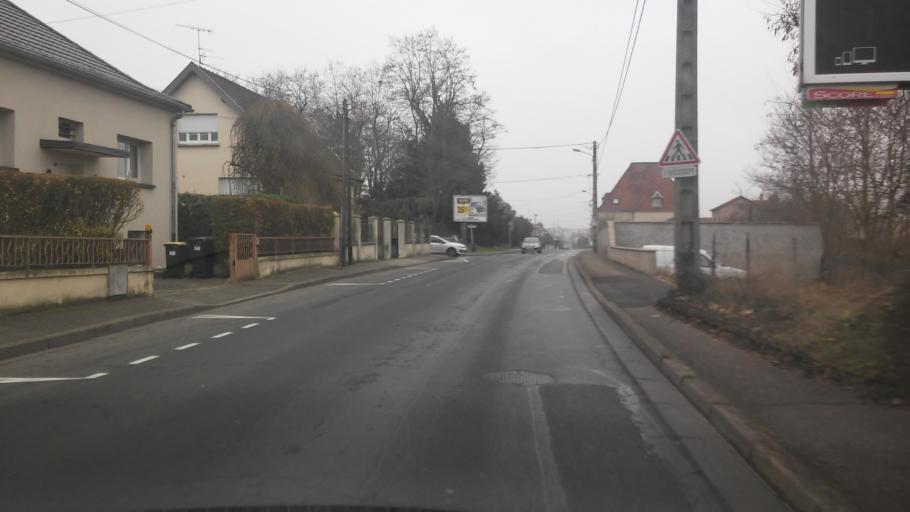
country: FR
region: Lorraine
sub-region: Departement de la Moselle
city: Montigny-les-Metz
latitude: 49.0916
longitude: 6.1744
